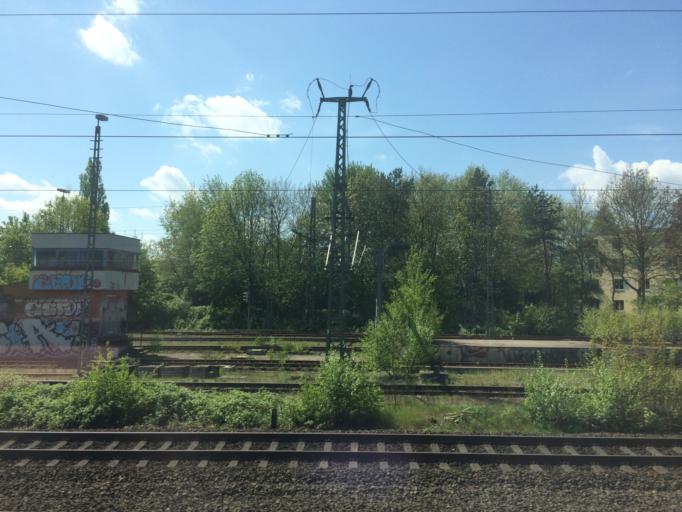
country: DE
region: Hamburg
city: Stellingen
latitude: 53.5919
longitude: 9.9146
